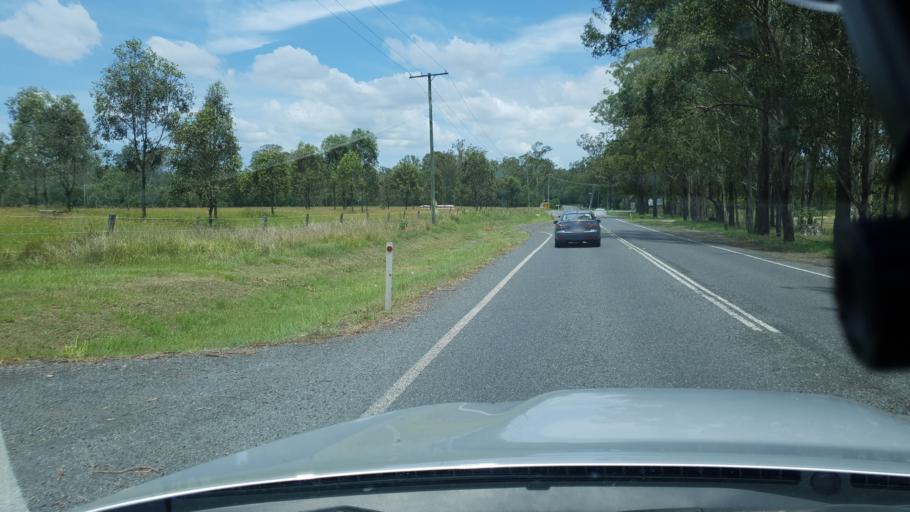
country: AU
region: Queensland
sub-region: Logan
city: North Maclean
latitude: -27.8269
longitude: 153.0129
